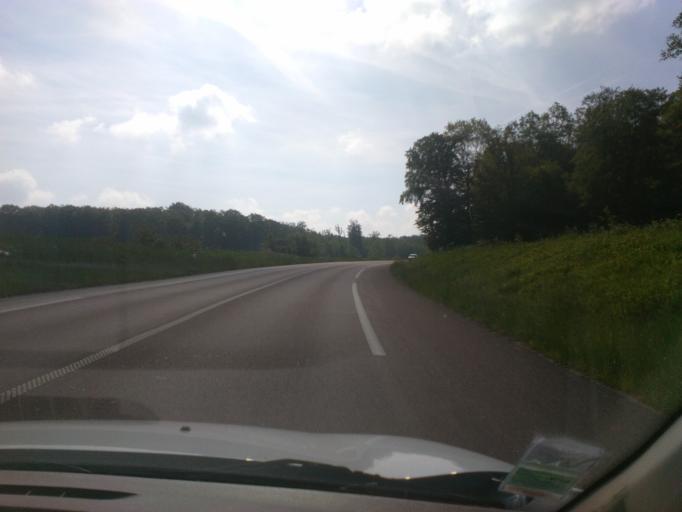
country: FR
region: Lorraine
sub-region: Departement des Vosges
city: Uxegney
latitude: 48.2050
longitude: 6.3879
